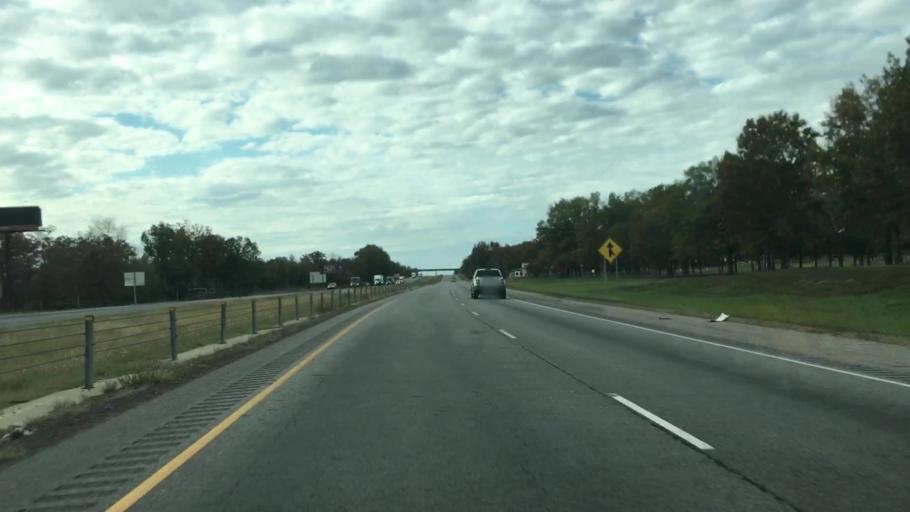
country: US
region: Arkansas
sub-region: Conway County
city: Morrilton
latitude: 35.1757
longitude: -92.7462
